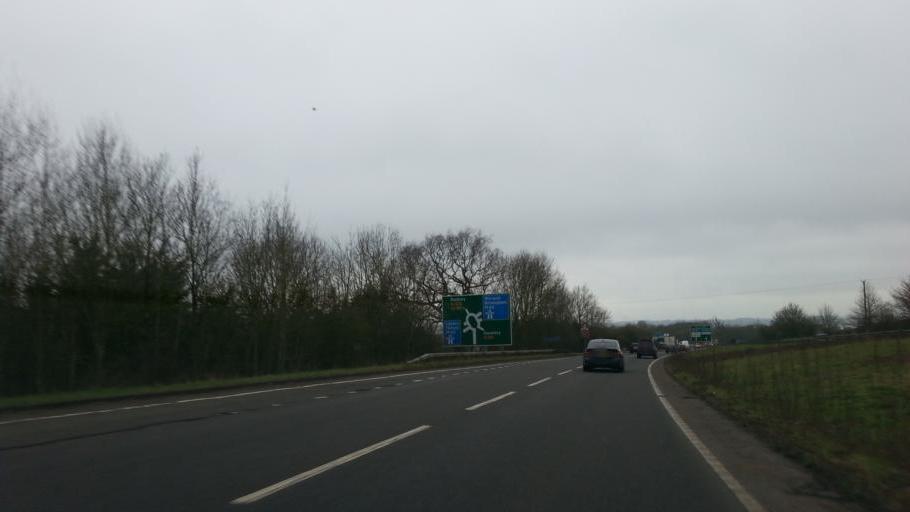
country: GB
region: England
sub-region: Oxfordshire
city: Banbury
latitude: 52.0710
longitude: -1.3051
